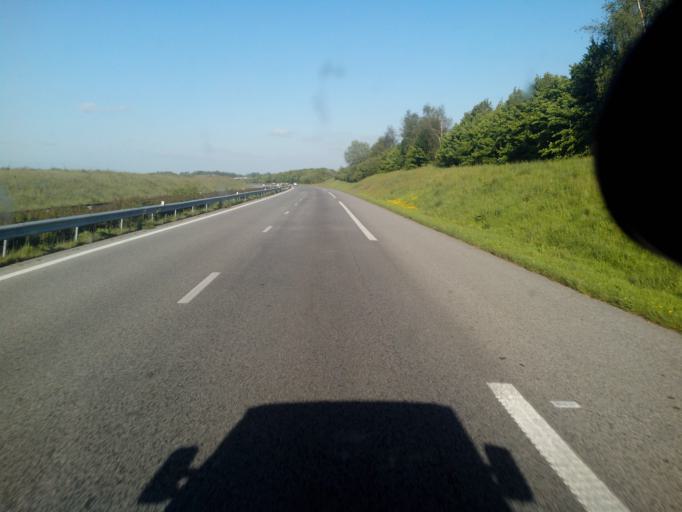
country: FR
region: Haute-Normandie
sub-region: Departement de la Seine-Maritime
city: Fauville-en-Caux
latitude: 49.6202
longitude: 0.5810
